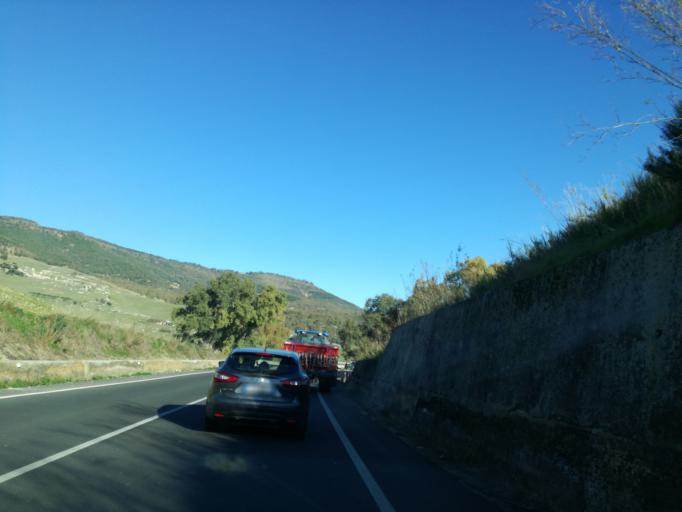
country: IT
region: Sicily
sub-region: Catania
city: San Michele di Ganzaria
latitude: 37.2374
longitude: 14.4500
